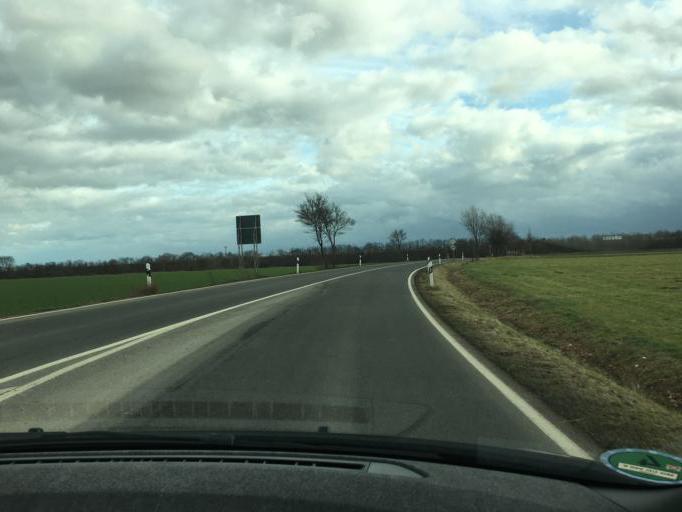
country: DE
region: North Rhine-Westphalia
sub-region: Regierungsbezirk Koln
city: Euskirchen
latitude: 50.6692
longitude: 6.7212
